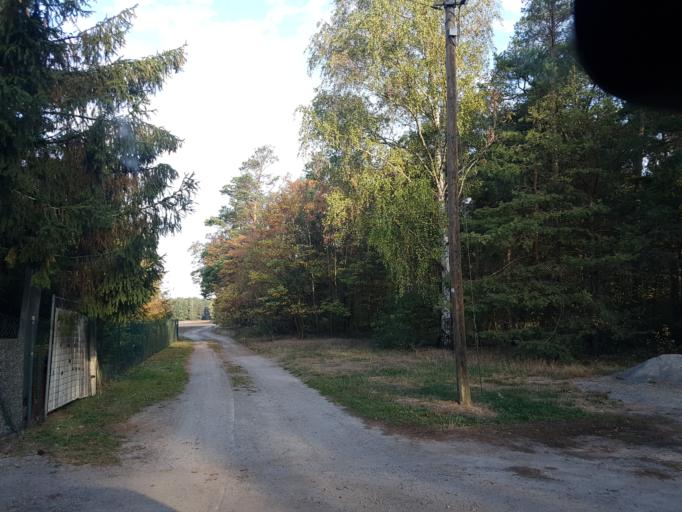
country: DE
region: Brandenburg
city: Finsterwalde
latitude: 51.5913
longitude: 13.7015
